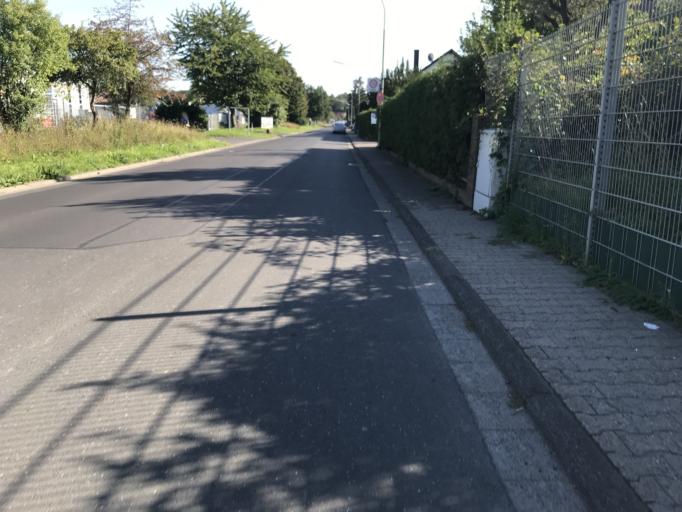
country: DE
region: Hesse
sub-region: Regierungsbezirk Darmstadt
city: Altenstadt
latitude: 50.2742
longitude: 8.9627
